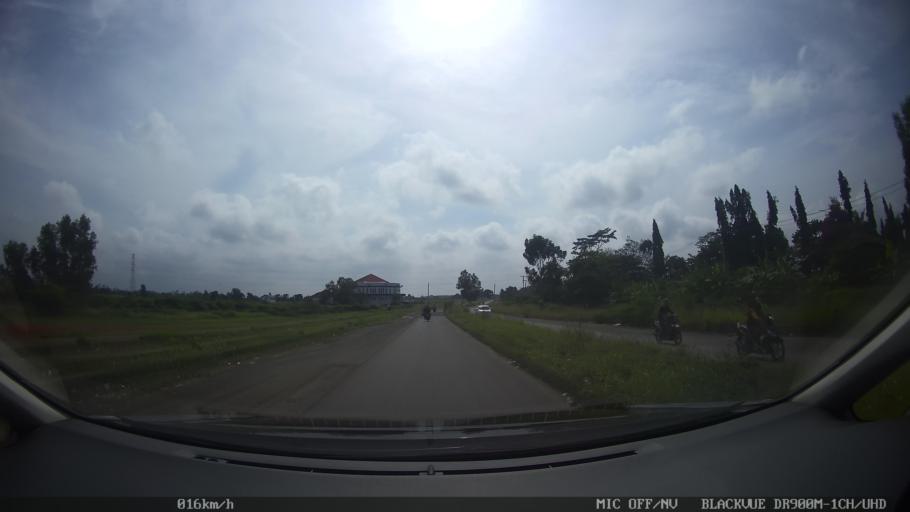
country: ID
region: Lampung
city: Kedaton
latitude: -5.3738
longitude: 105.3090
